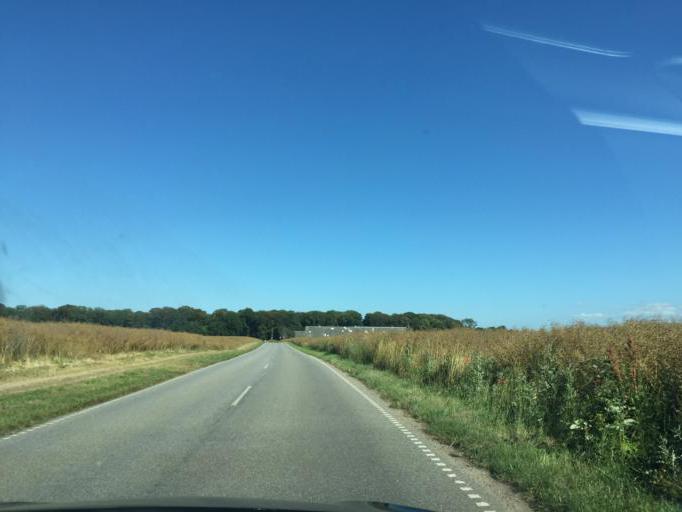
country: DK
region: South Denmark
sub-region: Nordfyns Kommune
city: Sonderso
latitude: 55.4858
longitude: 10.2682
